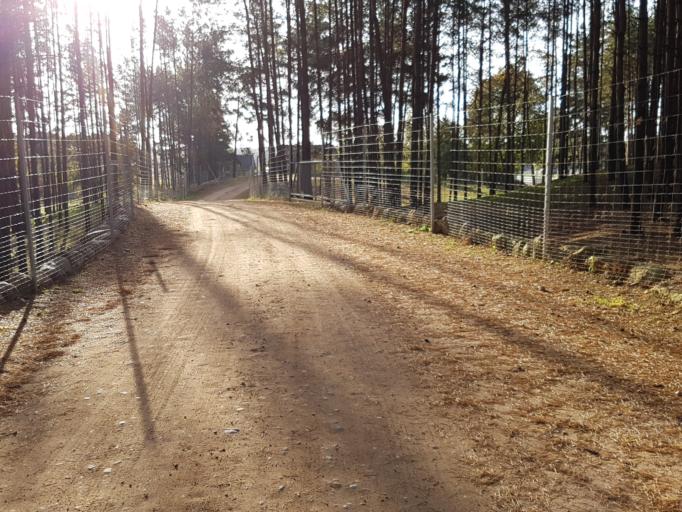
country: LT
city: Moletai
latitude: 55.0392
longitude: 25.4159
